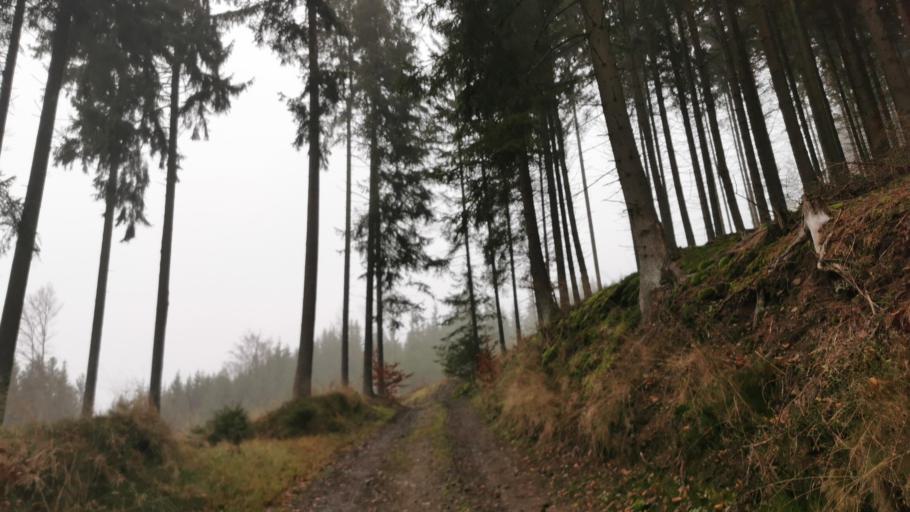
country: DE
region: Bavaria
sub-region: Upper Franconia
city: Ludwigsstadt
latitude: 50.4538
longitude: 11.3949
